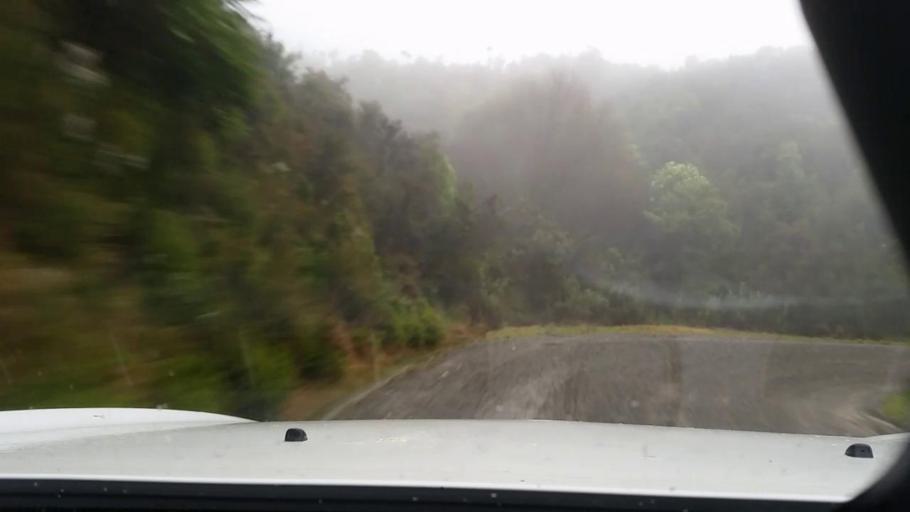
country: NZ
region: Wellington
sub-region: Masterton District
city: Masterton
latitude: -41.2436
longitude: 175.8764
